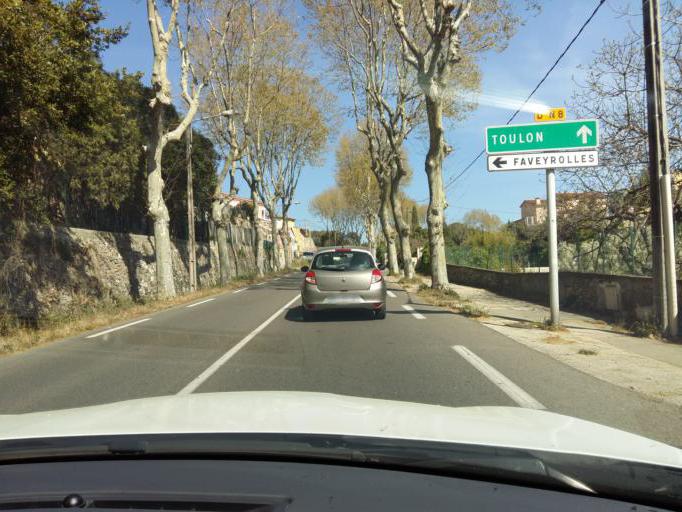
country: FR
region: Provence-Alpes-Cote d'Azur
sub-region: Departement du Var
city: Ollioules
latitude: 43.1352
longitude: 5.8552
